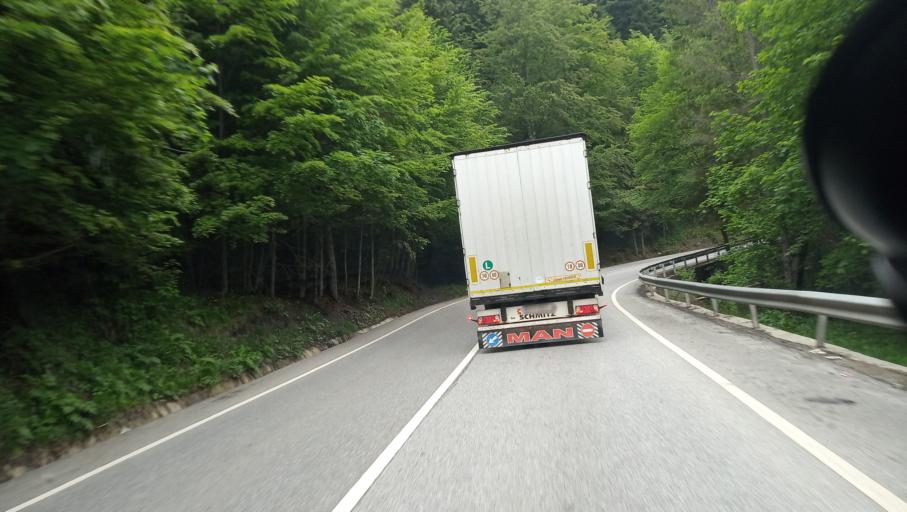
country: RO
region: Neamt
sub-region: Comuna Pipirig
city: Dolhesti
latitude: 47.1685
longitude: 26.0093
